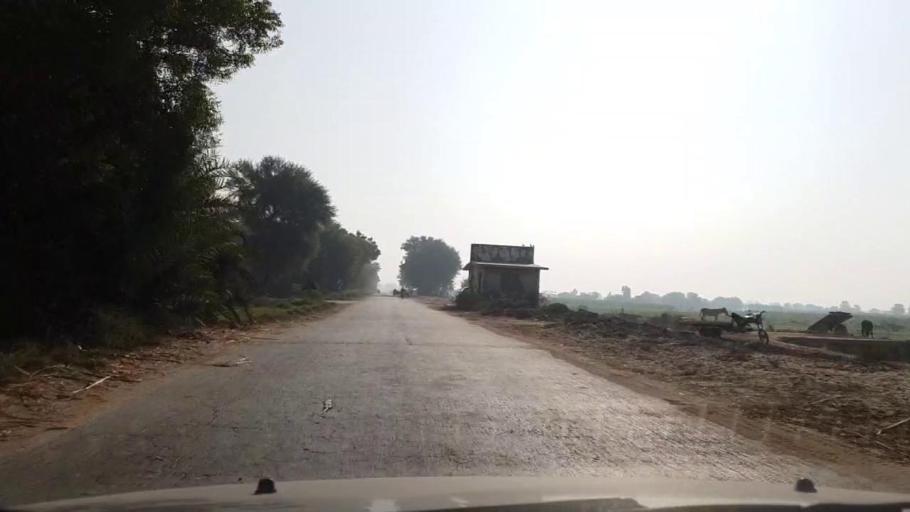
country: PK
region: Sindh
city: Matiari
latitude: 25.5898
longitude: 68.4778
